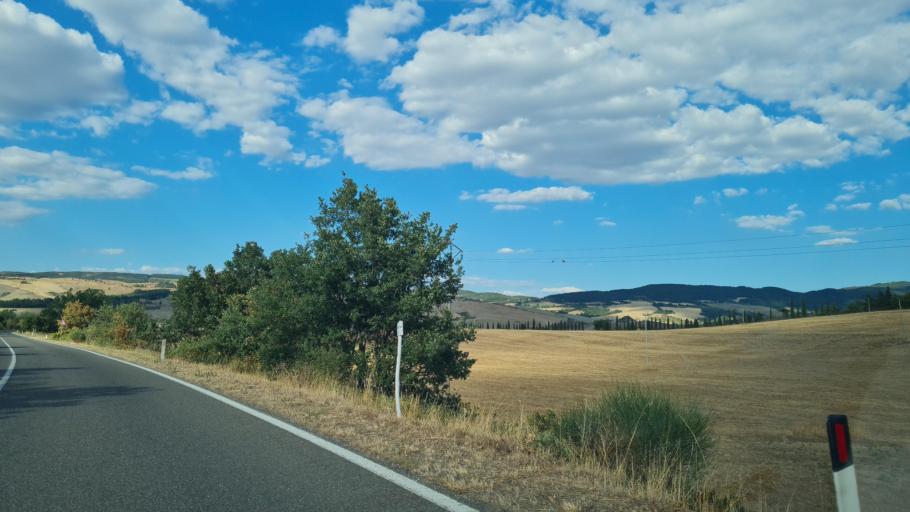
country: IT
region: Tuscany
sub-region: Provincia di Siena
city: Chianciano Terme
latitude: 43.0030
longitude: 11.7294
